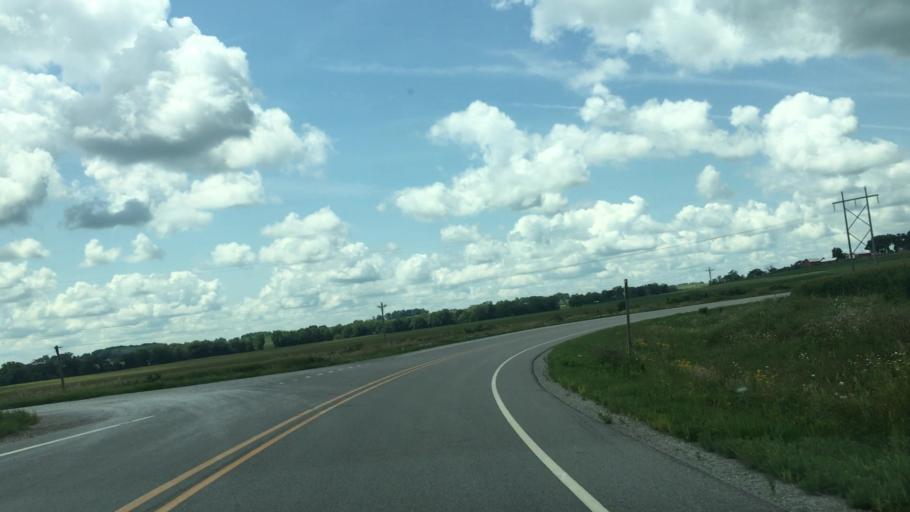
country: US
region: Iowa
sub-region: Johnson County
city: Solon
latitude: 41.8384
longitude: -91.4252
